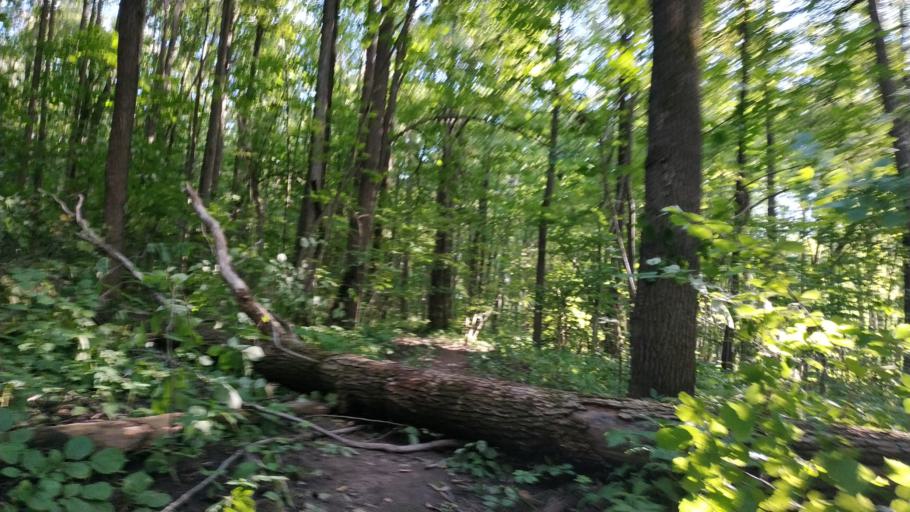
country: RU
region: Chuvashia
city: Novyye Lapsary
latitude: 56.1237
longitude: 47.1240
